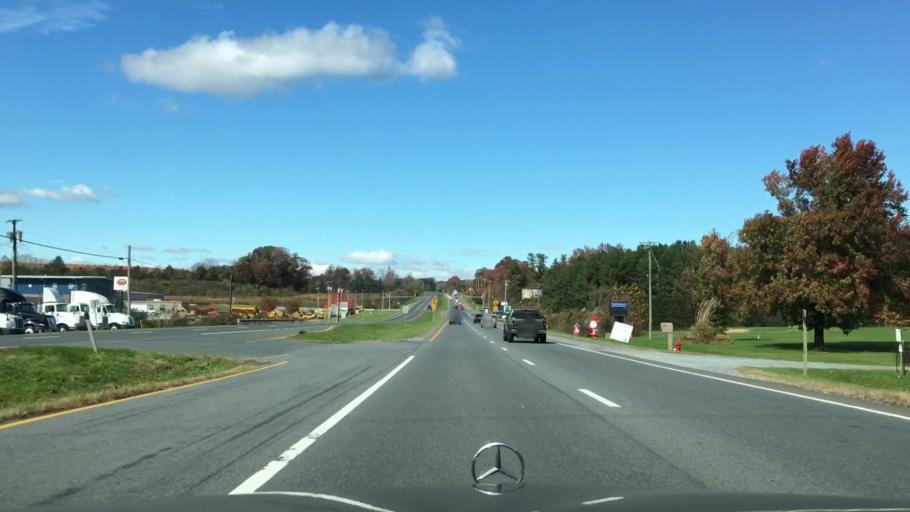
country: US
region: Virginia
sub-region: Campbell County
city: Timberlake
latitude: 37.3094
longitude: -79.1818
